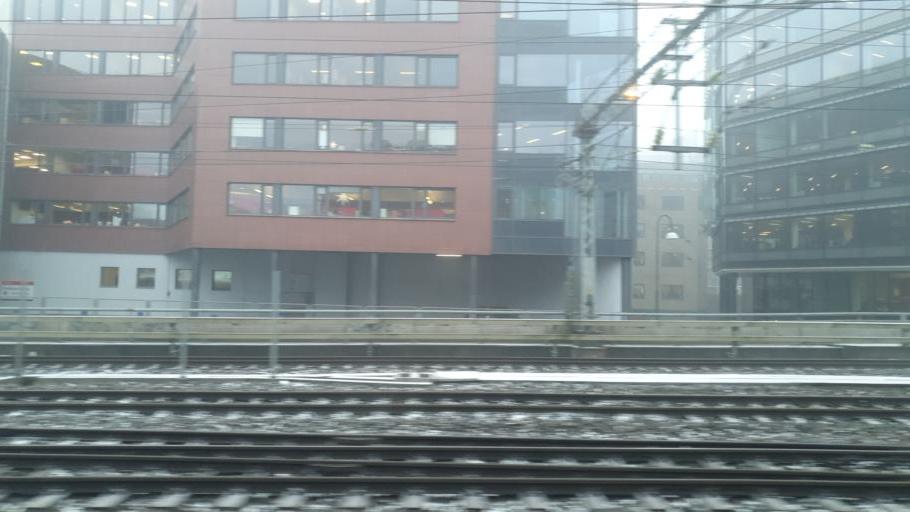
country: NO
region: Oslo
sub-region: Oslo
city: Sjolyststranda
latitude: 59.9213
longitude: 10.6826
